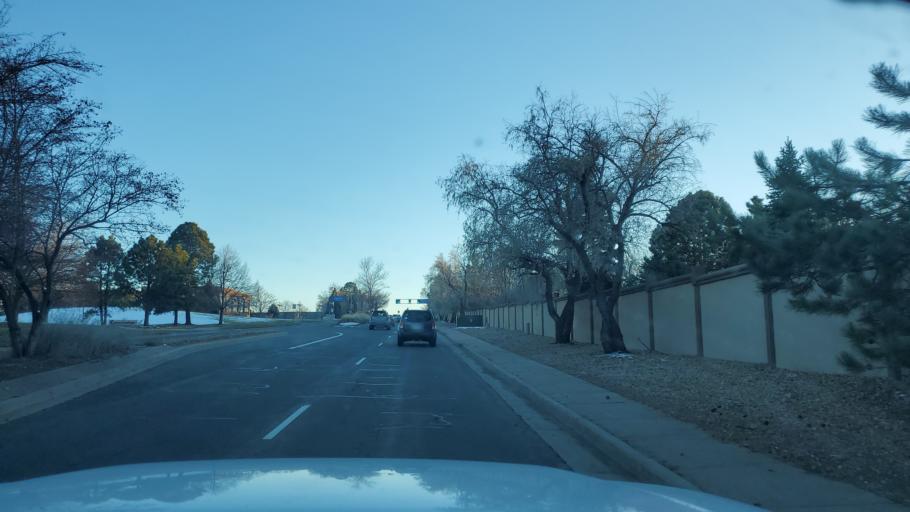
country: US
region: Colorado
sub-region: Arapahoe County
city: Castlewood
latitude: 39.6042
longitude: -104.9042
